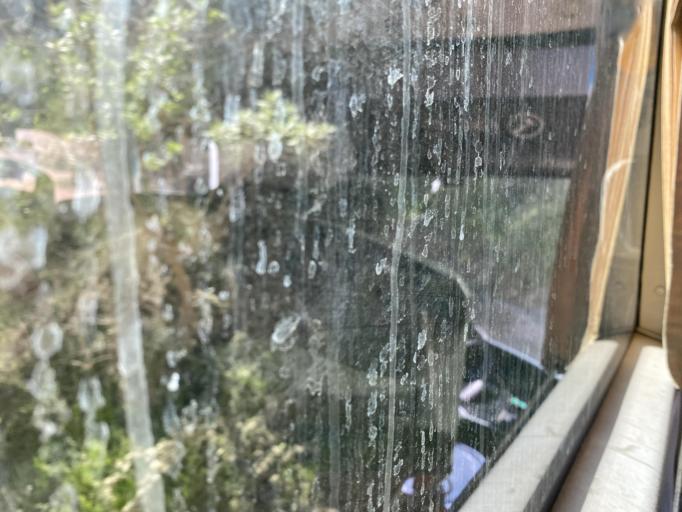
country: CL
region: Valparaiso
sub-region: Provincia de Marga Marga
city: Limache
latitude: -33.1982
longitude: -71.2645
